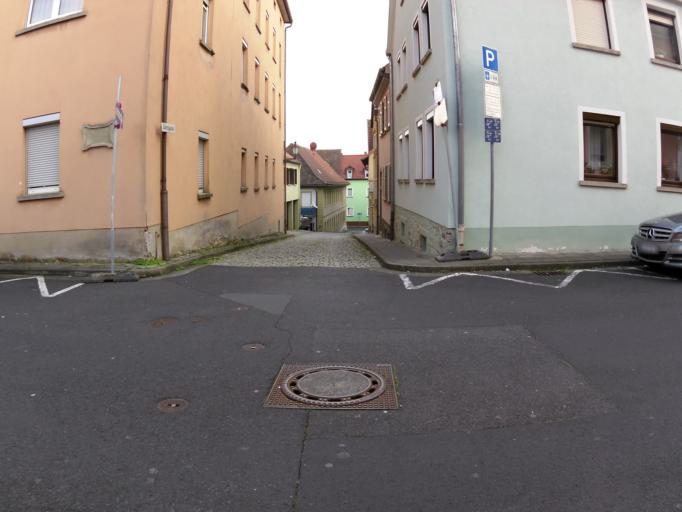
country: DE
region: Bavaria
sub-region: Regierungsbezirk Unterfranken
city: Kitzingen
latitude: 49.7389
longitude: 10.1583
